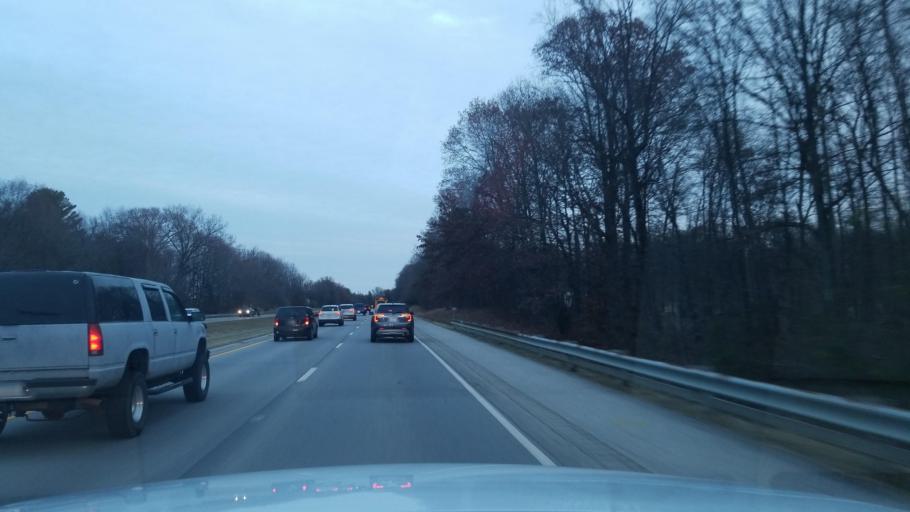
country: US
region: Indiana
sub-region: Vanderburgh County
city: Evansville
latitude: 37.9579
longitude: -87.6933
